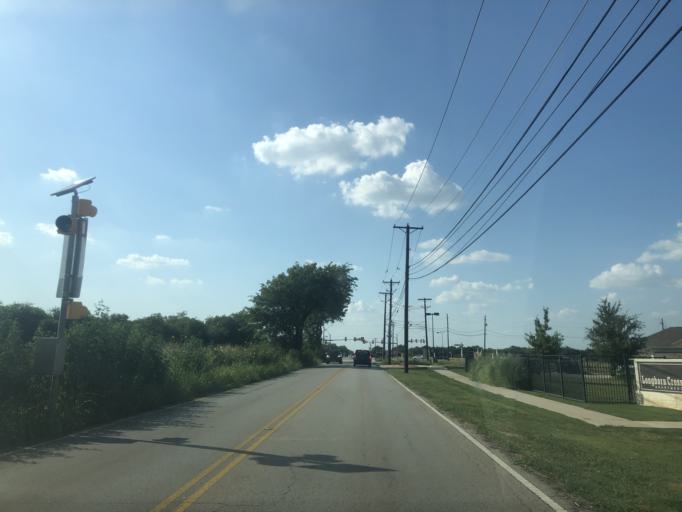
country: US
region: Texas
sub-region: Tarrant County
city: Saginaw
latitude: 32.8463
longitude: -97.3853
